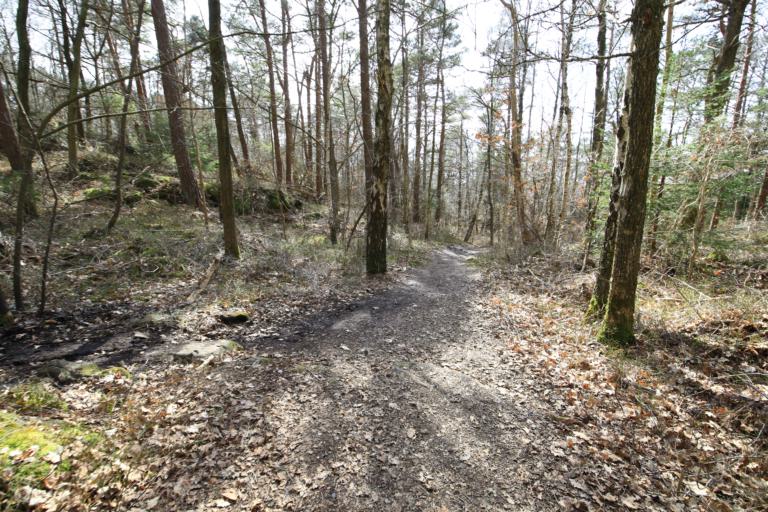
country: SE
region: Halland
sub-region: Varbergs Kommun
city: Varberg
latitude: 57.1465
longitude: 12.2845
